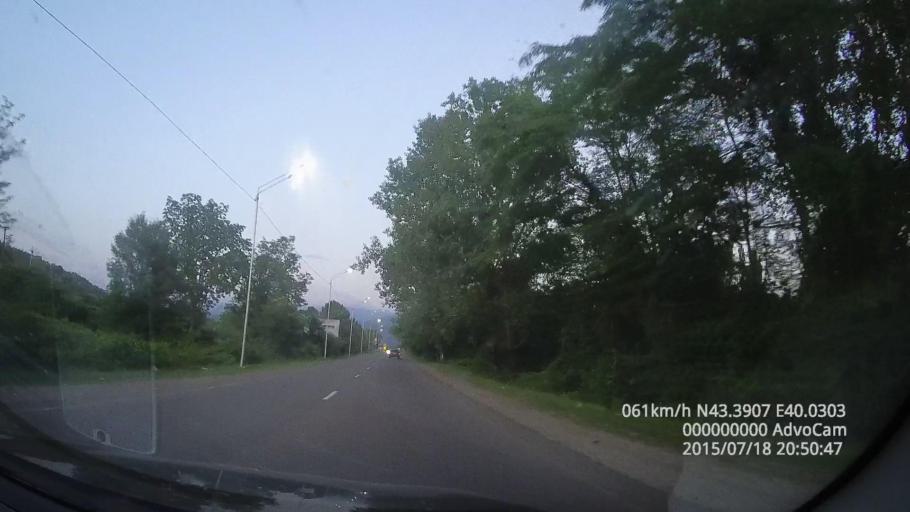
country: GE
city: Gantiadi
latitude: 43.3905
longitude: 40.0318
